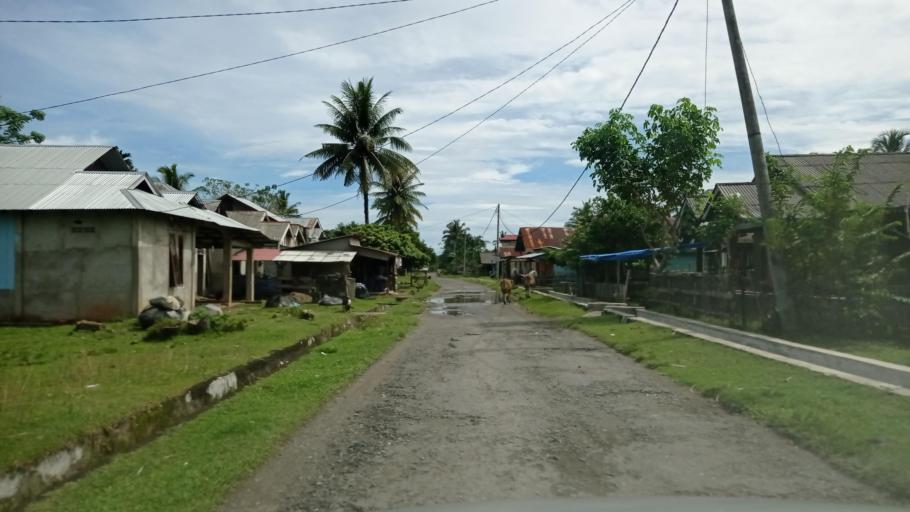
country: ID
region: Bengkulu
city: Ipuh
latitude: -2.5863
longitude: 101.1134
